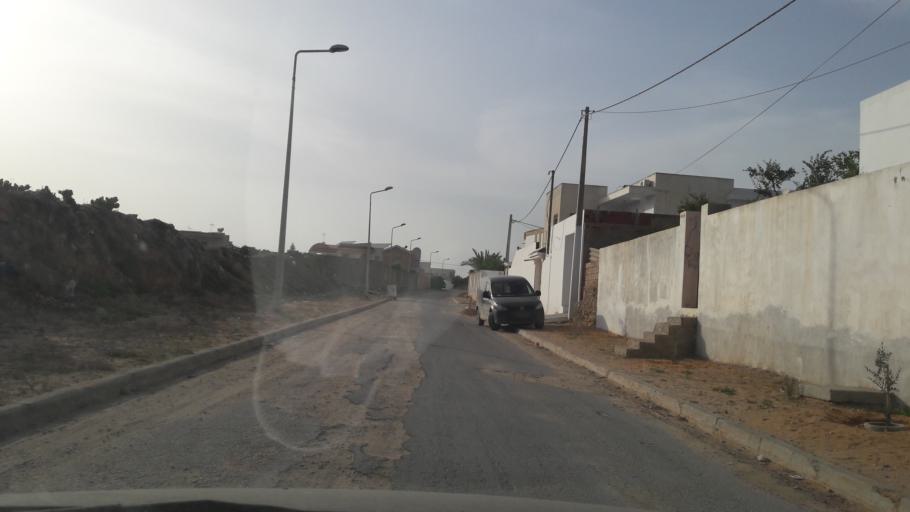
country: TN
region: Safaqis
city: Al Qarmadah
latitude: 34.8011
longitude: 10.7526
